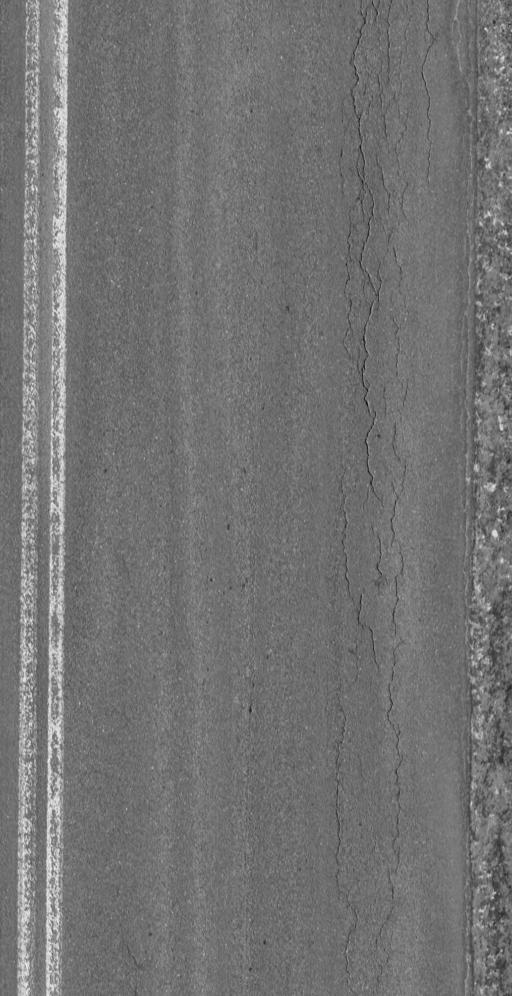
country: US
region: Vermont
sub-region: Windham County
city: Bellows Falls
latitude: 43.1108
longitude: -72.4591
